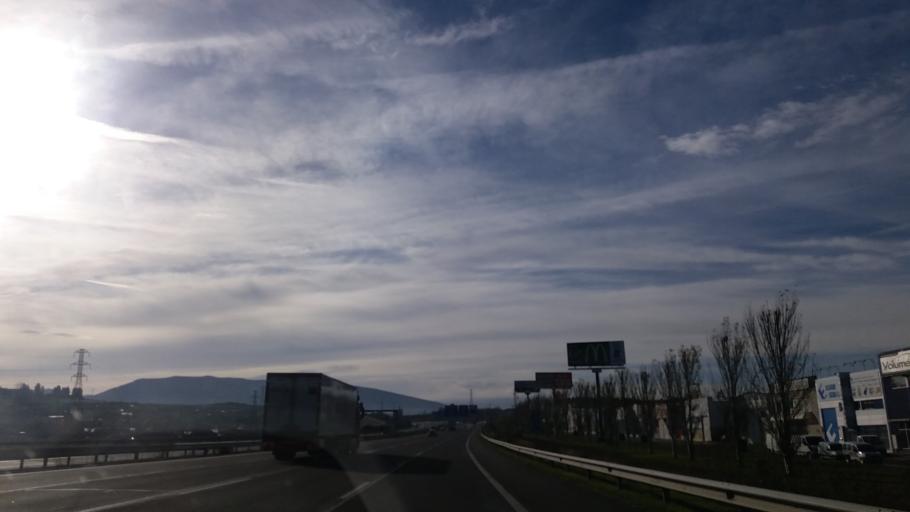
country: ES
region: Navarre
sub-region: Provincia de Navarra
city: Beriain
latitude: 42.7686
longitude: -1.6303
